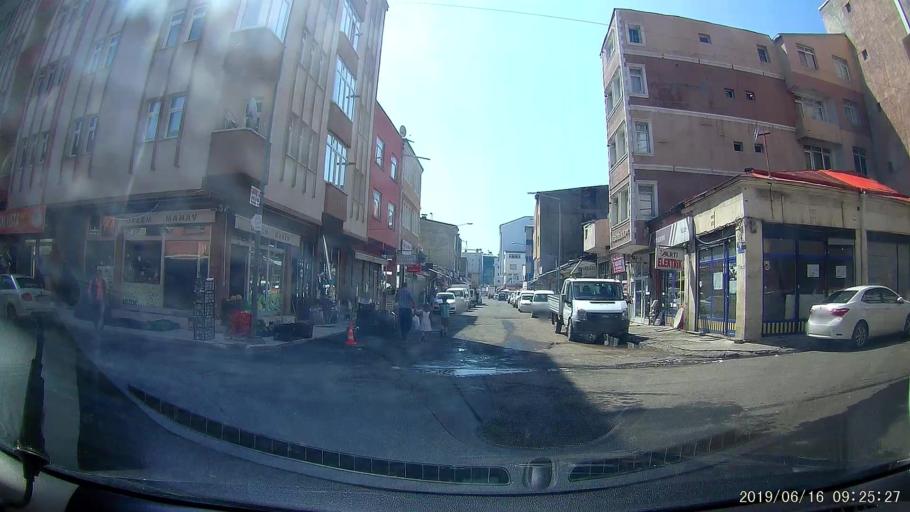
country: TR
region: Kars
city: Kars
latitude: 40.6089
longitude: 43.0957
